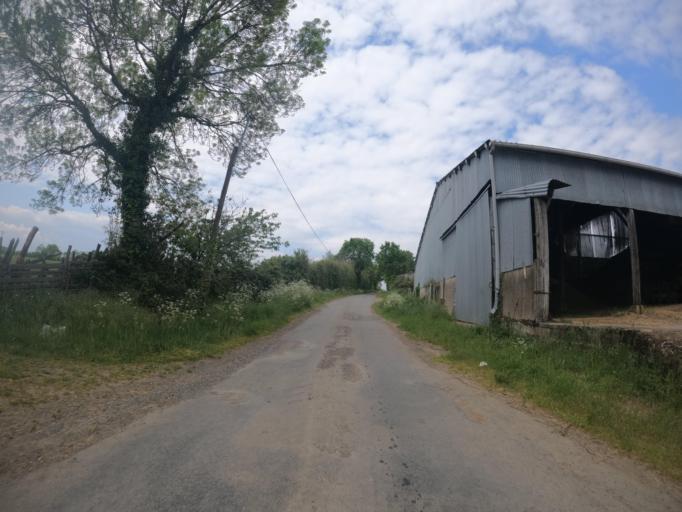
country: FR
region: Poitou-Charentes
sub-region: Departement des Deux-Sevres
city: Saint-Varent
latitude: 46.8750
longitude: -0.2794
